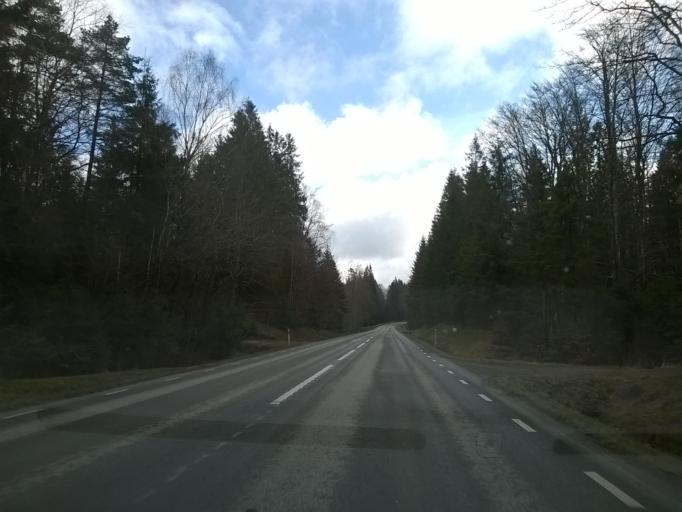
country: SE
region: Vaestra Goetaland
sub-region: Marks Kommun
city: Horred
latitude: 57.1557
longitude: 12.6504
